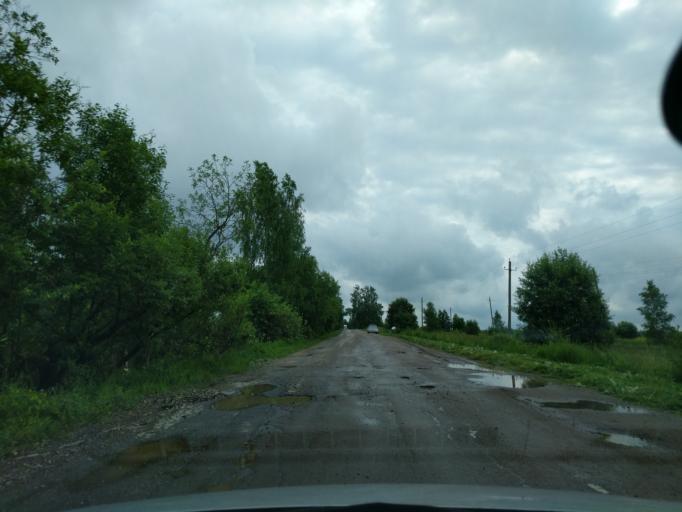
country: RU
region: Kaluga
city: Myatlevo
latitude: 54.7854
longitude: 35.7325
